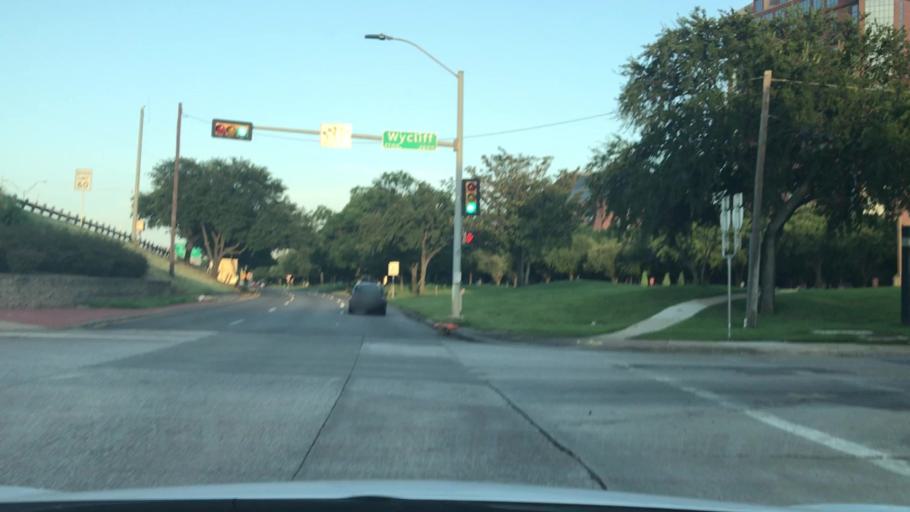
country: US
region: Texas
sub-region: Dallas County
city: Dallas
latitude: 32.8023
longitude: -96.8322
